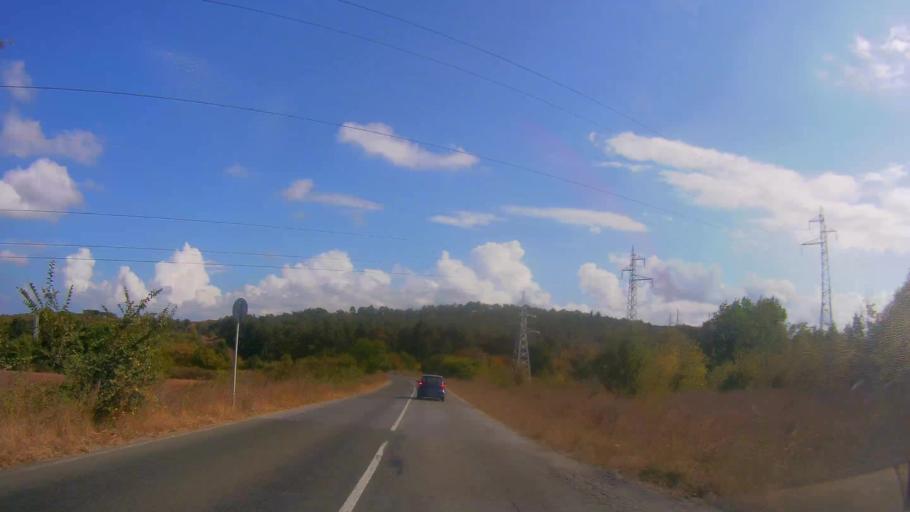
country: BG
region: Burgas
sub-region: Obshtina Burgas
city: Burgas
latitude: 42.4752
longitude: 27.3965
